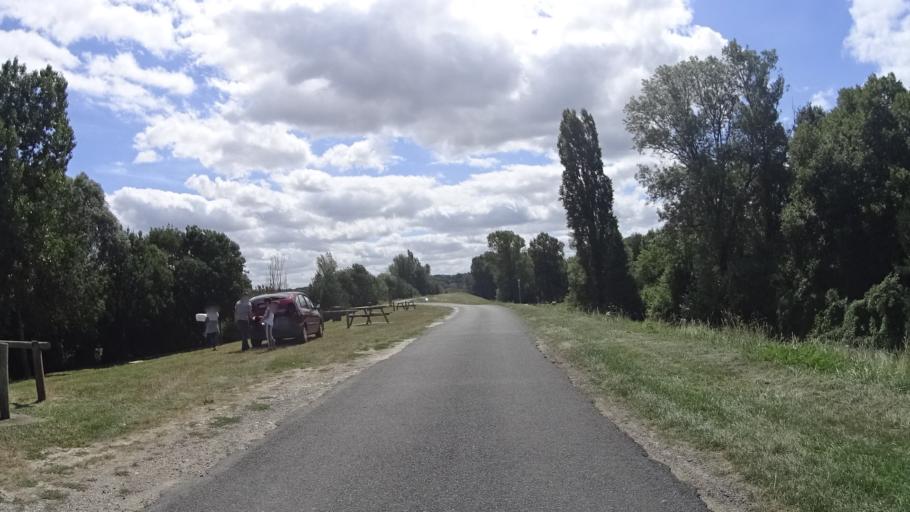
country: FR
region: Centre
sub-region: Departement d'Indre-et-Loire
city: Cinq-Mars-la-Pile
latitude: 47.3416
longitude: 0.4806
